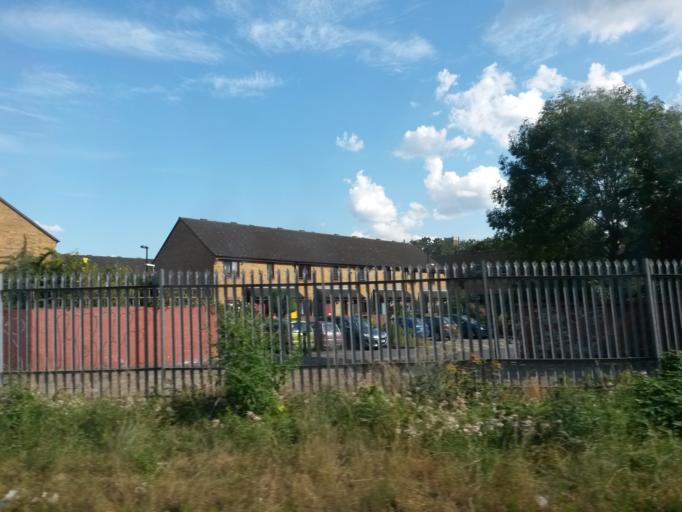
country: GB
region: England
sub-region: Greater London
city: Croydon
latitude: 51.3836
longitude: -0.0962
